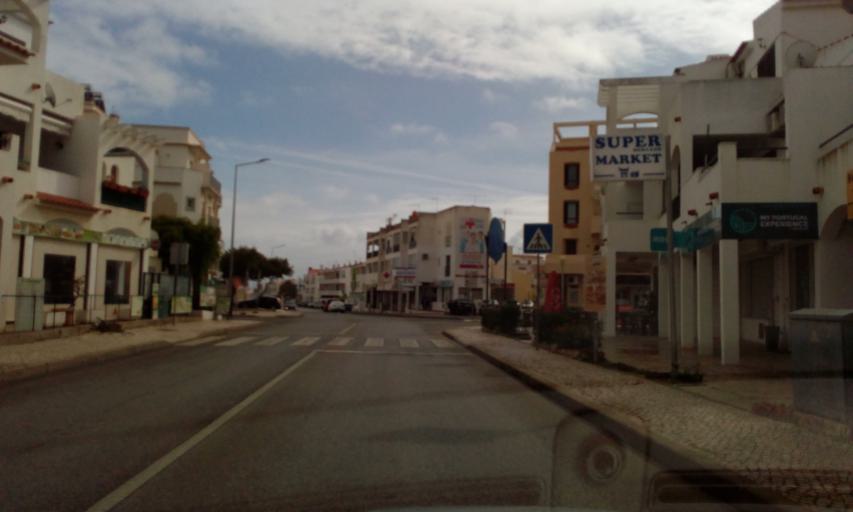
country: PT
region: Faro
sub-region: Albufeira
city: Albufeira
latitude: 37.0944
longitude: -8.2241
